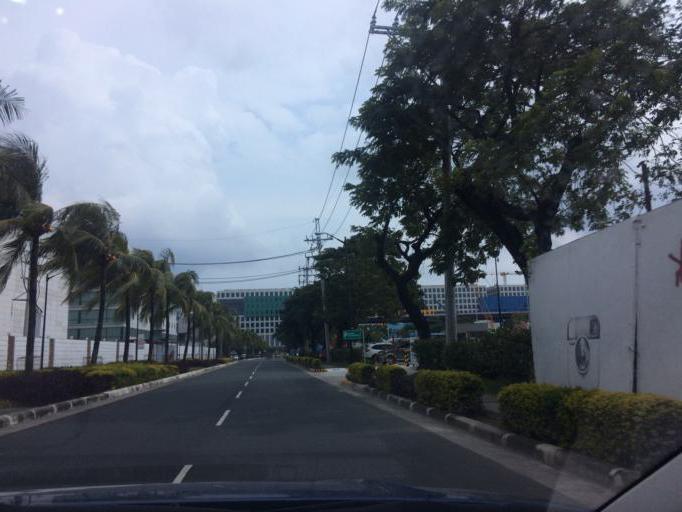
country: PH
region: Metro Manila
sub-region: Makati City
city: Makati City
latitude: 14.5398
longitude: 120.9905
